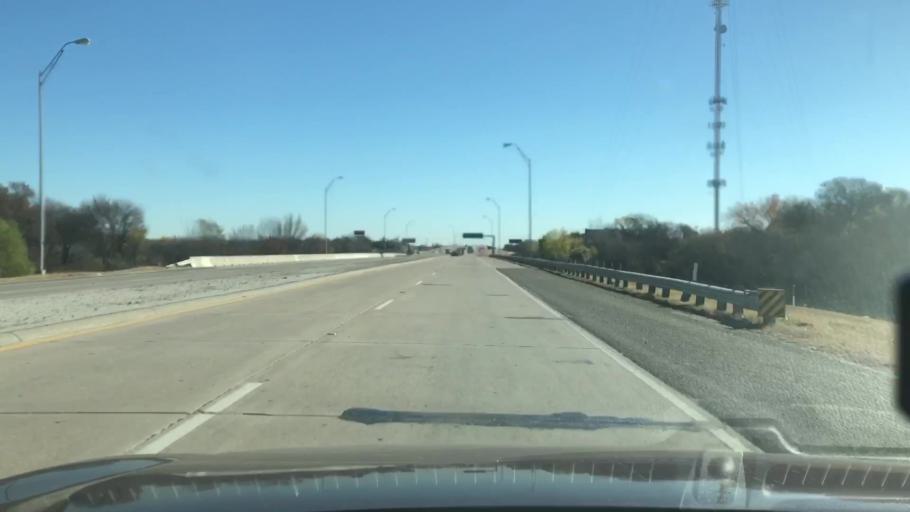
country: US
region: Texas
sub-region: Dallas County
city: Farmers Branch
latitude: 32.8725
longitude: -96.9262
